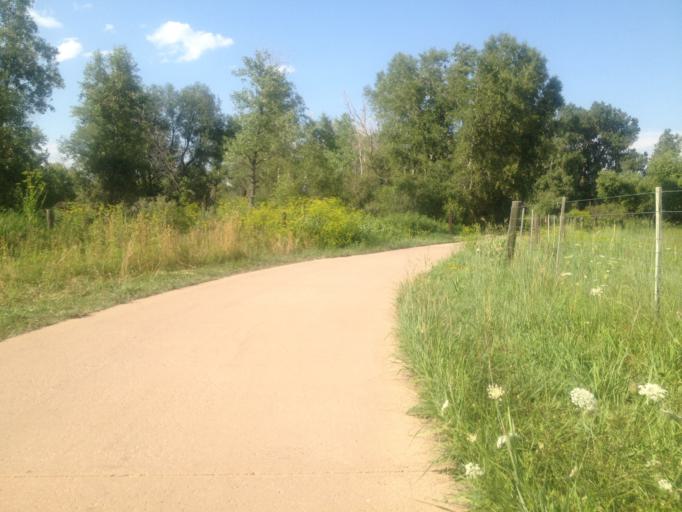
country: US
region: Colorado
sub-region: Boulder County
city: Boulder
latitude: 39.9961
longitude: -105.2157
